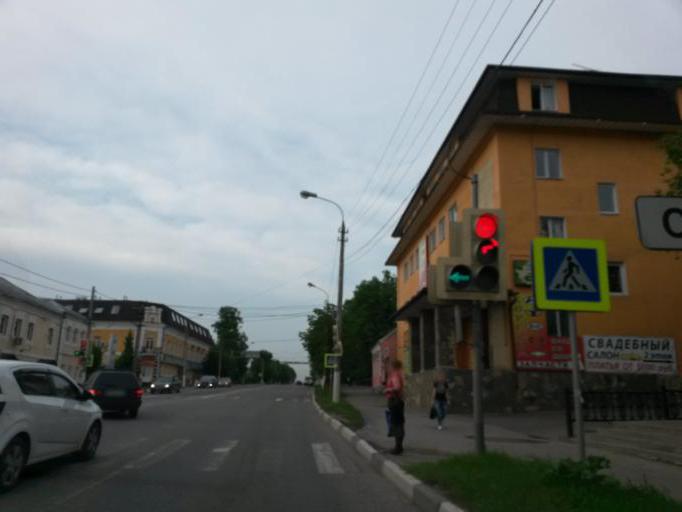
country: RU
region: Moskovskaya
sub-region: Chekhovskiy Rayon
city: Chekhov
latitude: 55.1442
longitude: 37.4533
